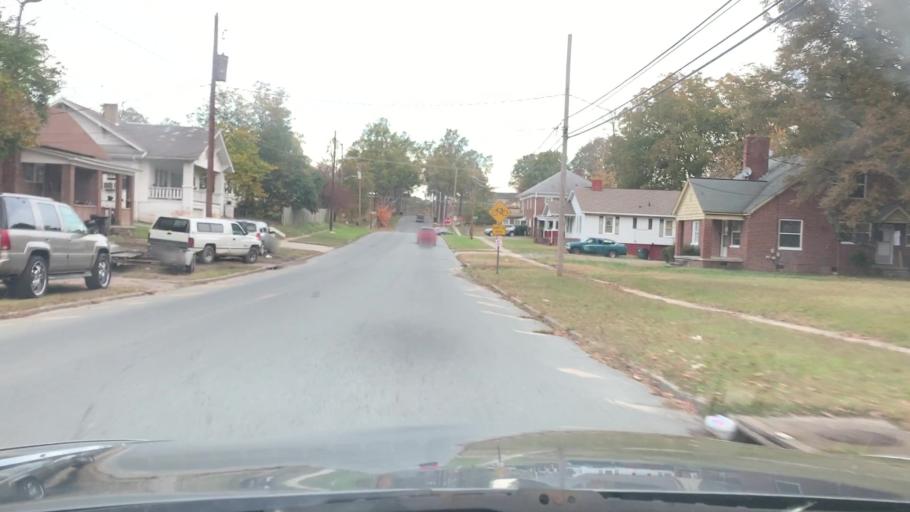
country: US
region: North Carolina
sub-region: Alamance County
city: Burlington
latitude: 36.0965
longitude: -79.4292
